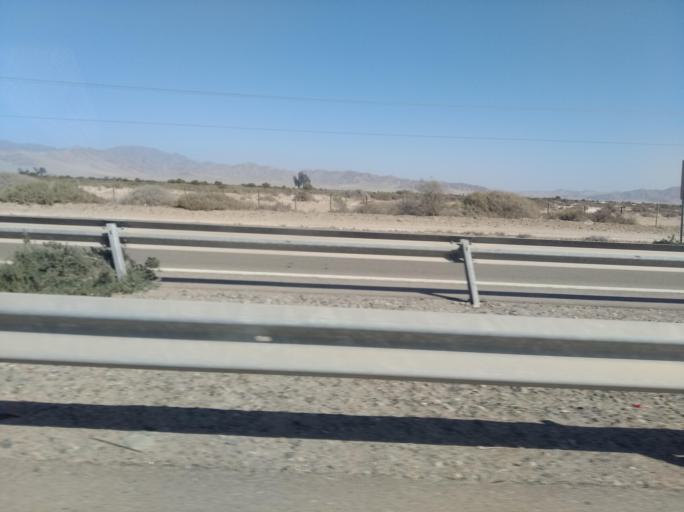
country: CL
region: Atacama
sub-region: Provincia de Copiapo
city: Copiapo
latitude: -27.3501
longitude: -70.6433
